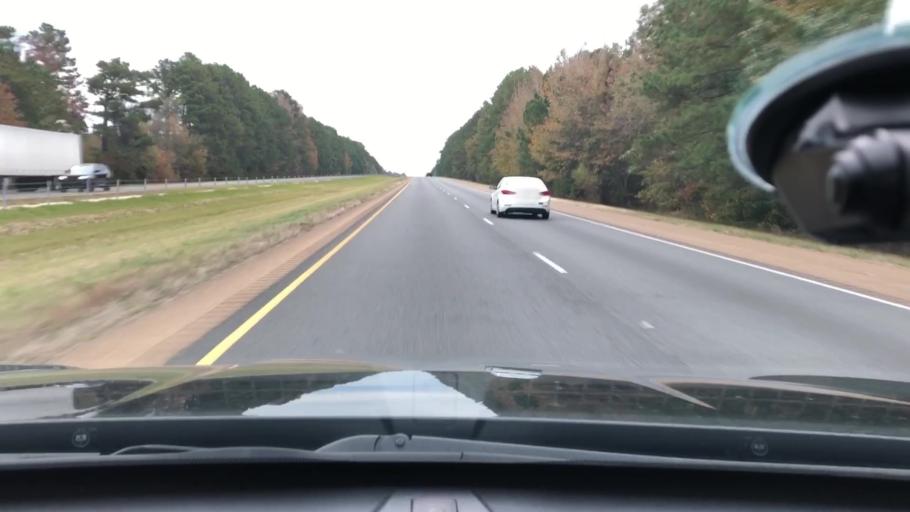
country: US
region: Arkansas
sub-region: Clark County
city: Gurdon
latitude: 33.9730
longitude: -93.2073
